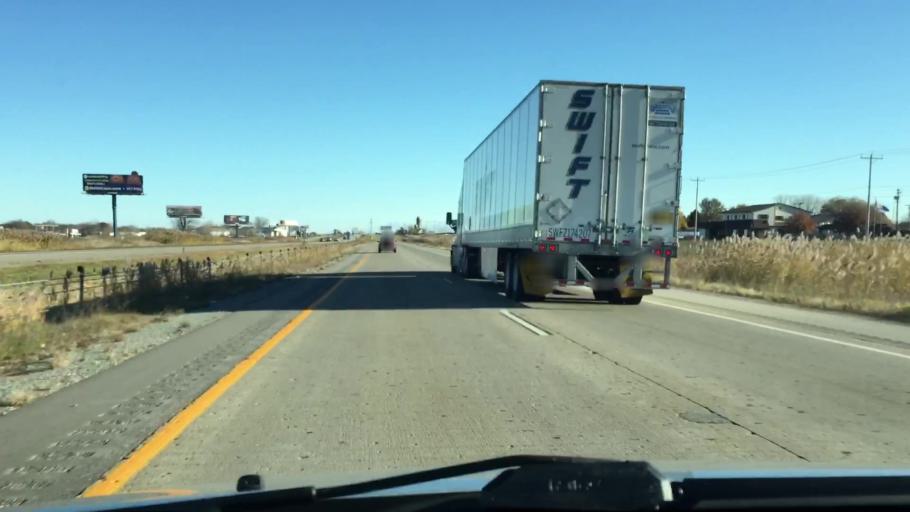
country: US
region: Wisconsin
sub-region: Outagamie County
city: Kaukauna
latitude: 44.3161
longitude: -88.2257
